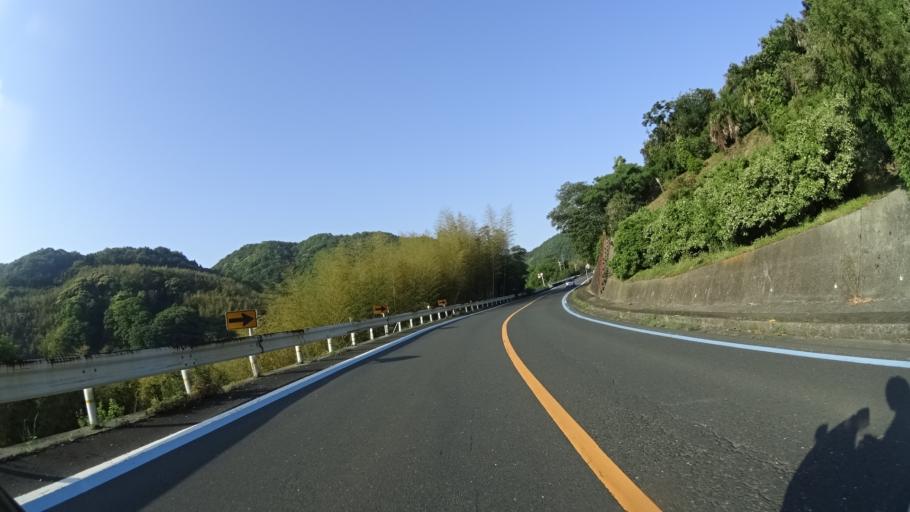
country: JP
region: Ehime
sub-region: Nishiuwa-gun
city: Ikata-cho
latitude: 33.4834
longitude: 132.3346
